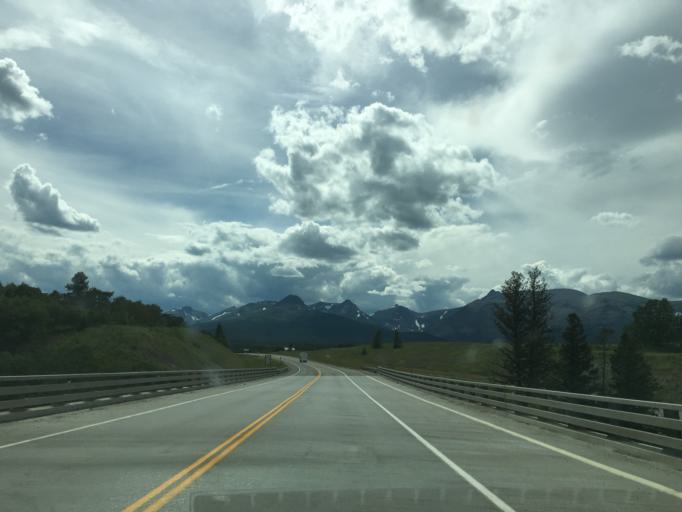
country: US
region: Montana
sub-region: Glacier County
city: South Browning
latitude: 48.4499
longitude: -113.2073
